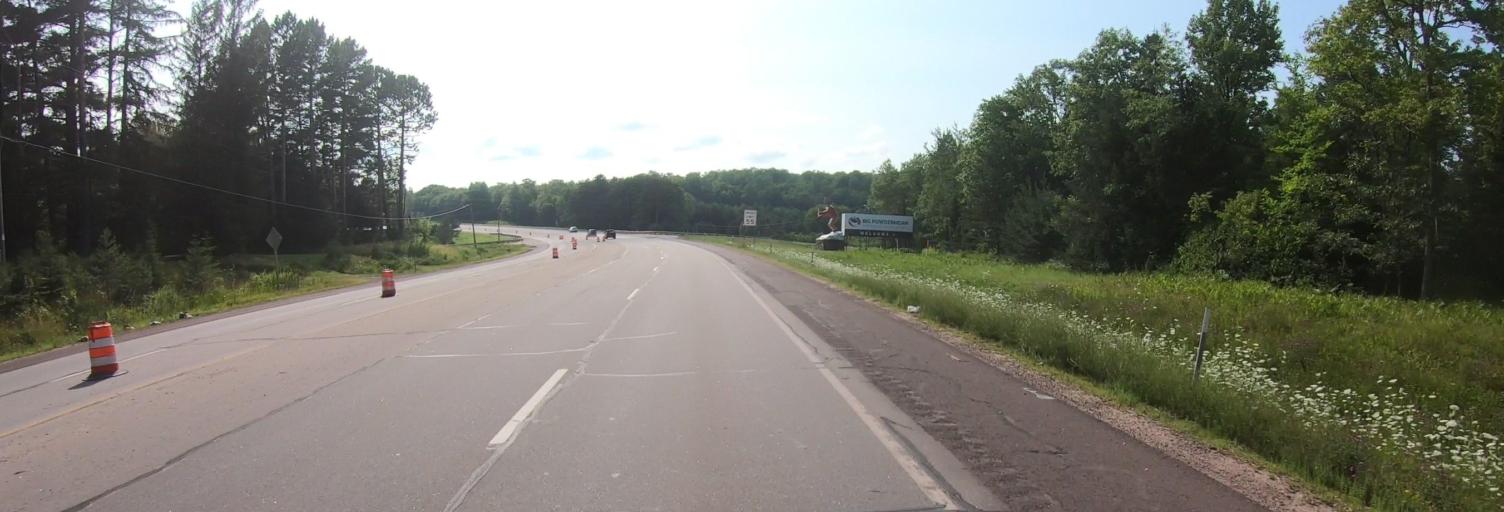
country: US
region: Michigan
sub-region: Gogebic County
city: Bessemer
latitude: 46.4814
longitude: -90.0813
